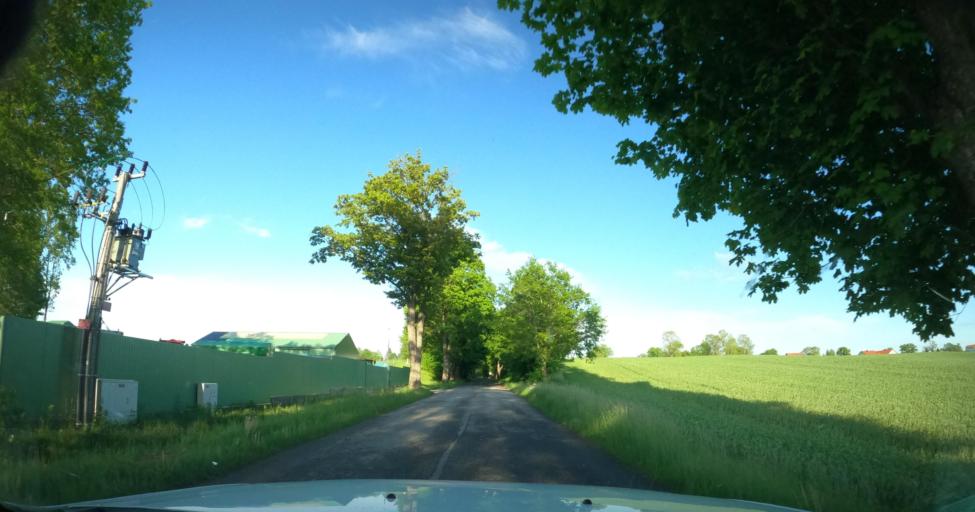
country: PL
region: Warmian-Masurian Voivodeship
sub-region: Powiat braniewski
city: Braniewo
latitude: 54.2814
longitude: 19.8706
